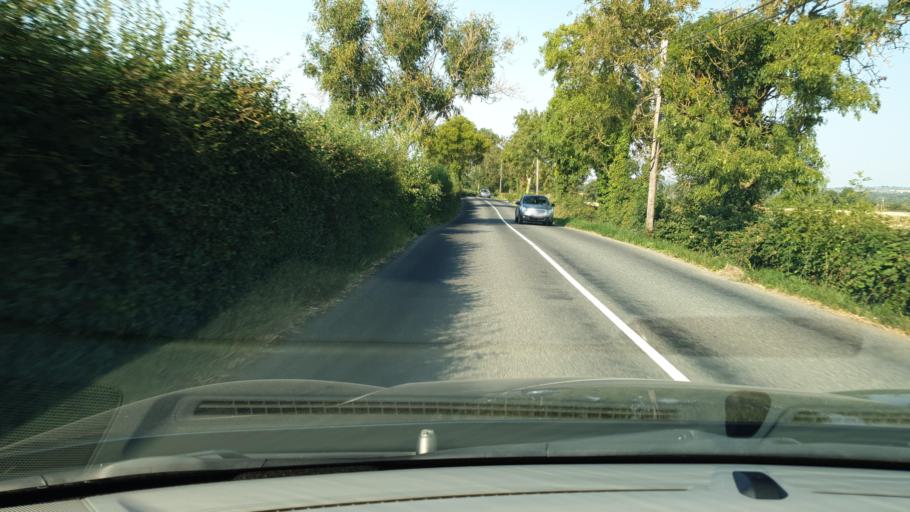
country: IE
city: Kentstown
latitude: 53.5991
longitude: -6.4795
